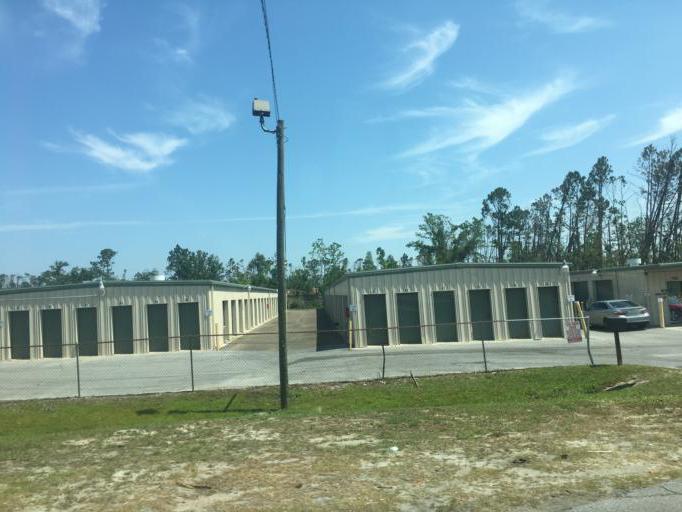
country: US
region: Florida
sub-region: Bay County
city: Lynn Haven
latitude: 30.2187
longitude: -85.6583
